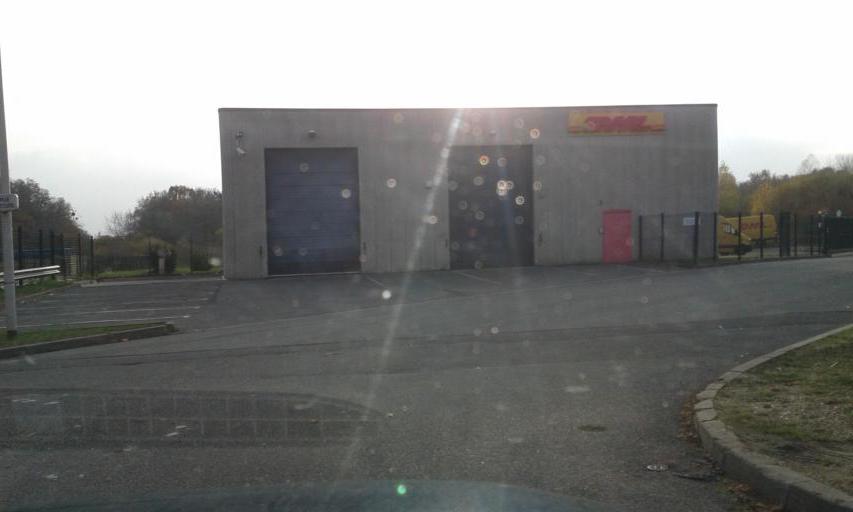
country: FR
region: Centre
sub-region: Departement du Loiret
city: Saran
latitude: 47.9484
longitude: 1.8598
